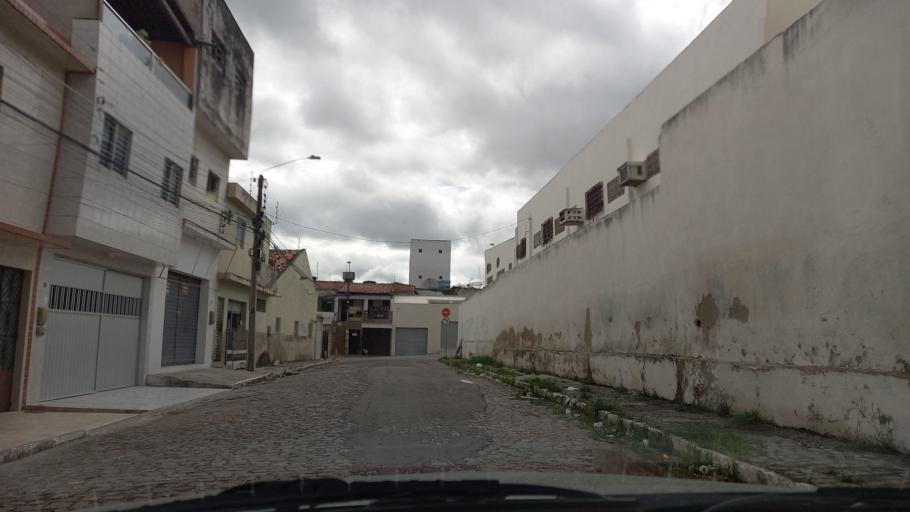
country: BR
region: Pernambuco
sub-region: Caruaru
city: Caruaru
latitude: -8.2797
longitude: -35.9789
